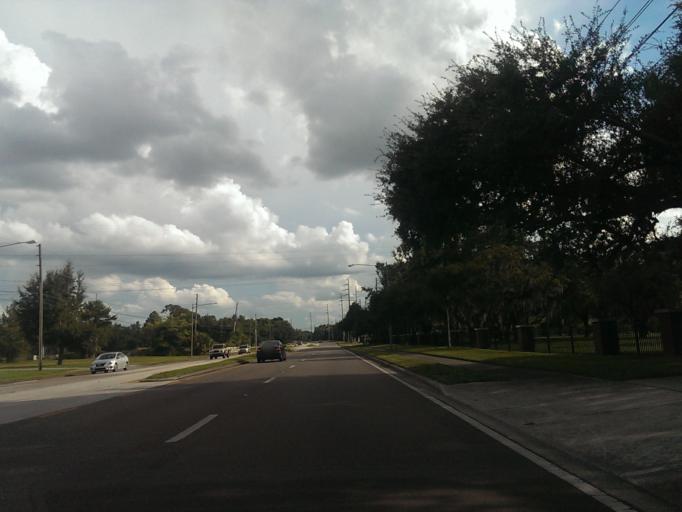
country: US
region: Florida
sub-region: Orange County
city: Bay Hill
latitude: 28.4793
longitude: -81.5085
